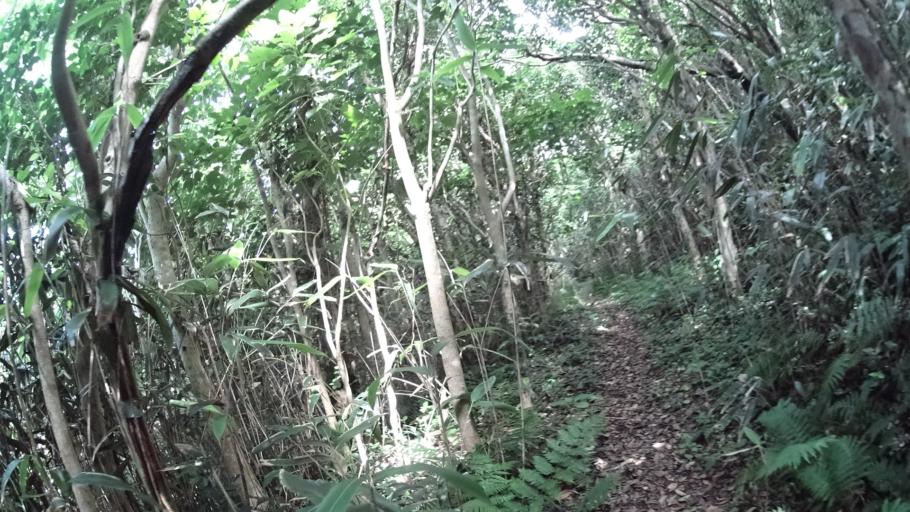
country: JP
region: Shizuoka
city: Shimoda
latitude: 34.5180
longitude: 139.2765
